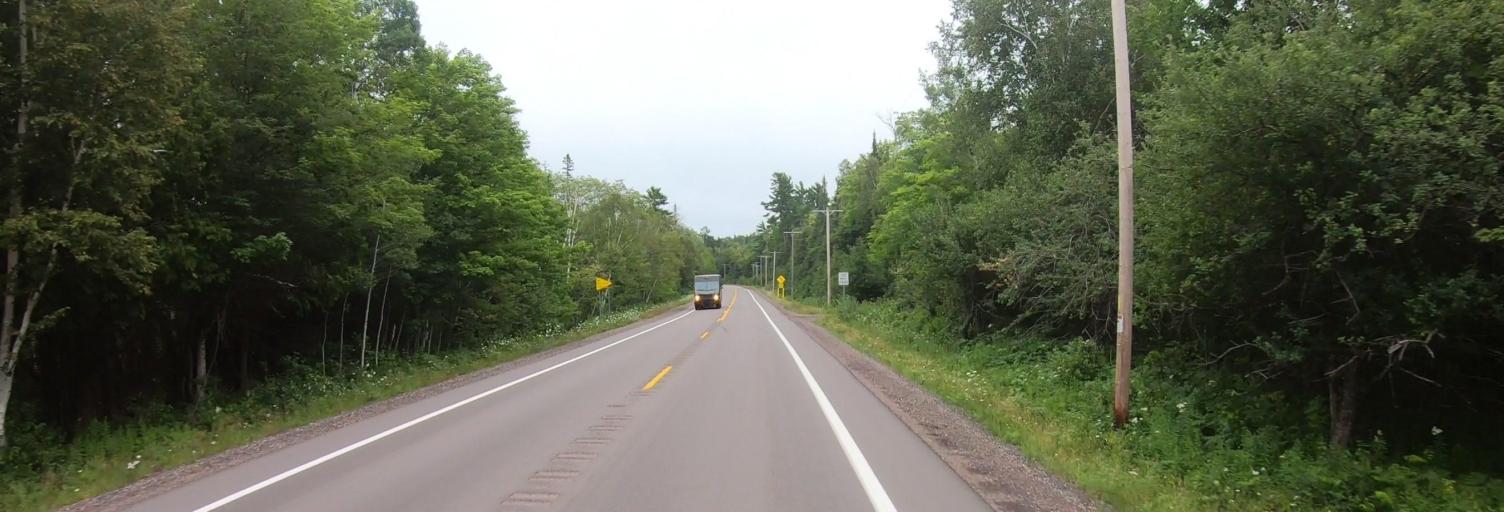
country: US
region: Michigan
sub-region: Keweenaw County
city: Eagle River
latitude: 47.3985
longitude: -88.2867
